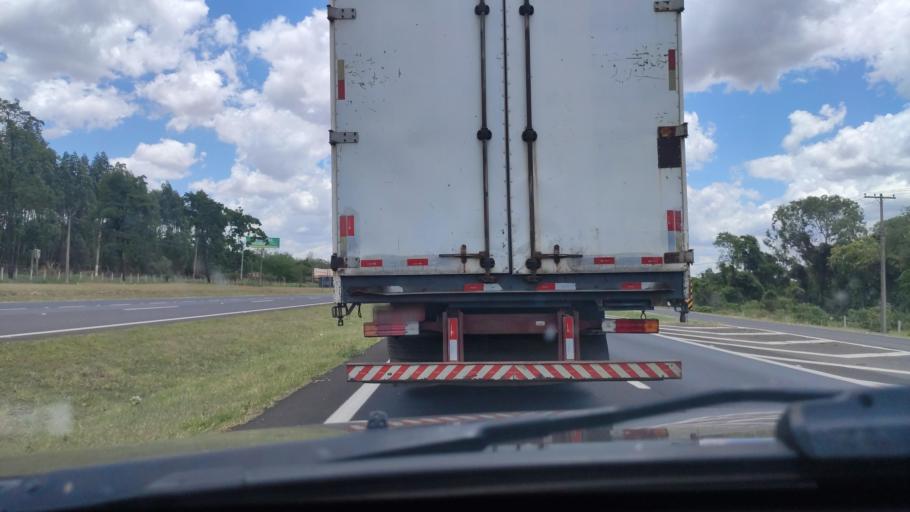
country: BR
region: Sao Paulo
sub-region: Bauru
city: Bauru
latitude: -22.3208
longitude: -48.9730
